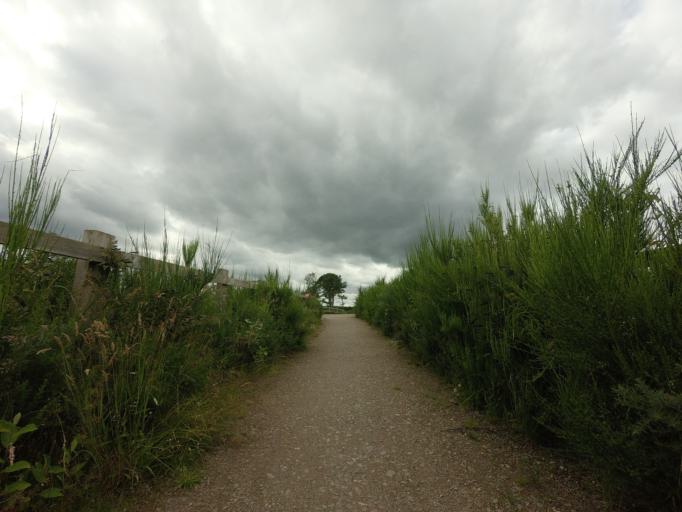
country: GB
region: Scotland
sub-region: Moray
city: Forres
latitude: 57.6114
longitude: -3.6393
